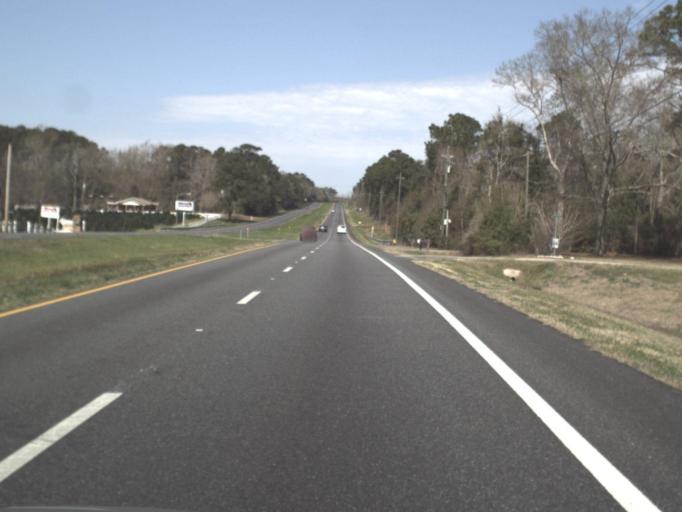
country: US
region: Florida
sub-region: Gadsden County
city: Havana
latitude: 30.5900
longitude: -84.4053
